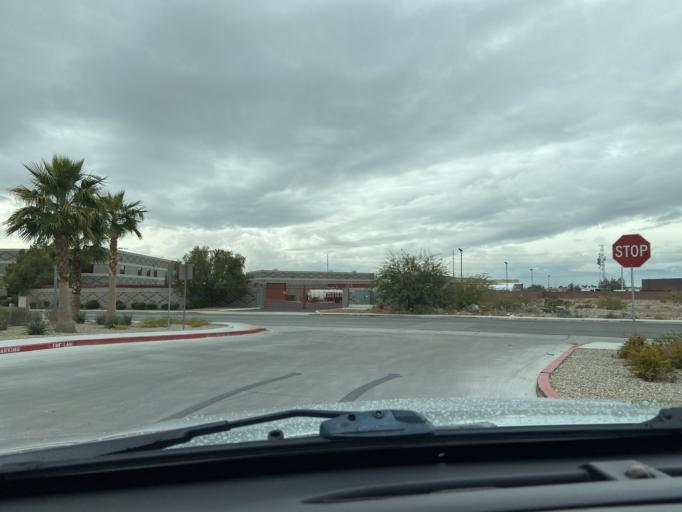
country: US
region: Nevada
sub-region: Clark County
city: North Las Vegas
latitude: 36.2456
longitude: -115.1120
